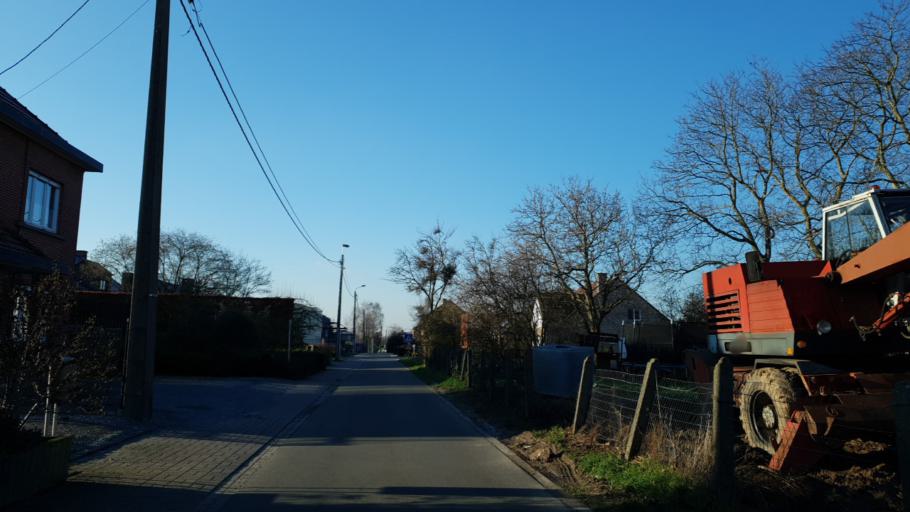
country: BE
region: Flanders
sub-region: Provincie Vlaams-Brabant
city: Herent
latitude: 50.9211
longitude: 4.6806
